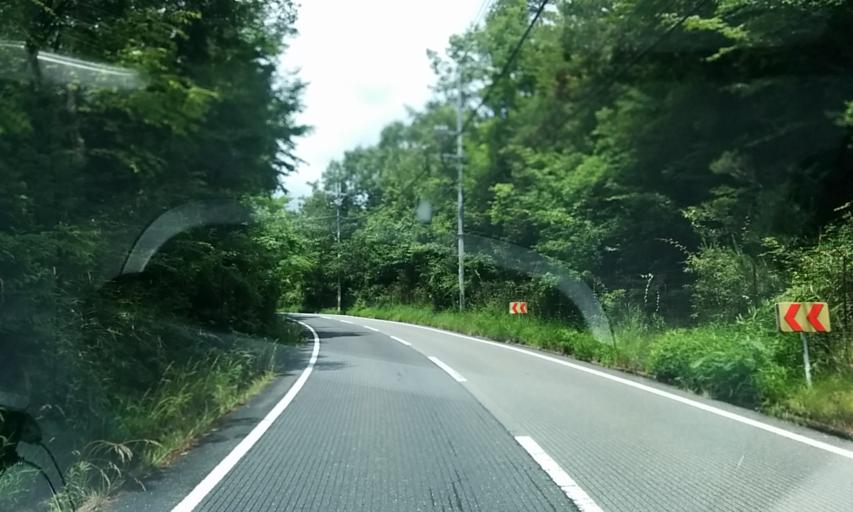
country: JP
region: Kyoto
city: Kameoka
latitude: 35.0081
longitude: 135.4702
